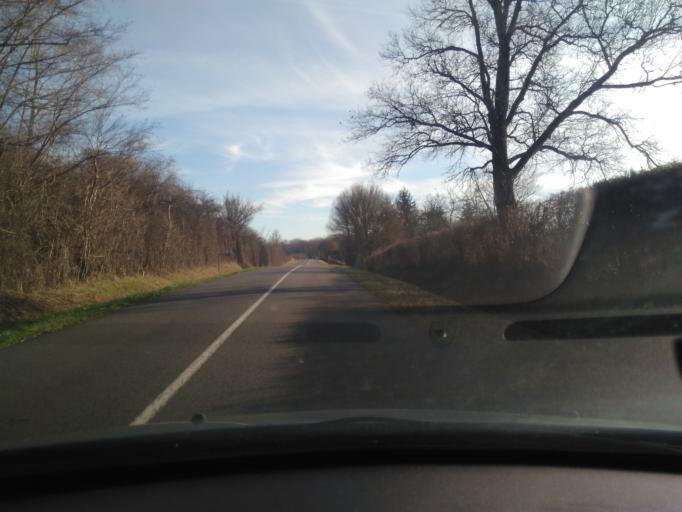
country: FR
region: Centre
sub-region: Departement du Cher
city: Le Chatelet
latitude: 46.6348
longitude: 2.2105
